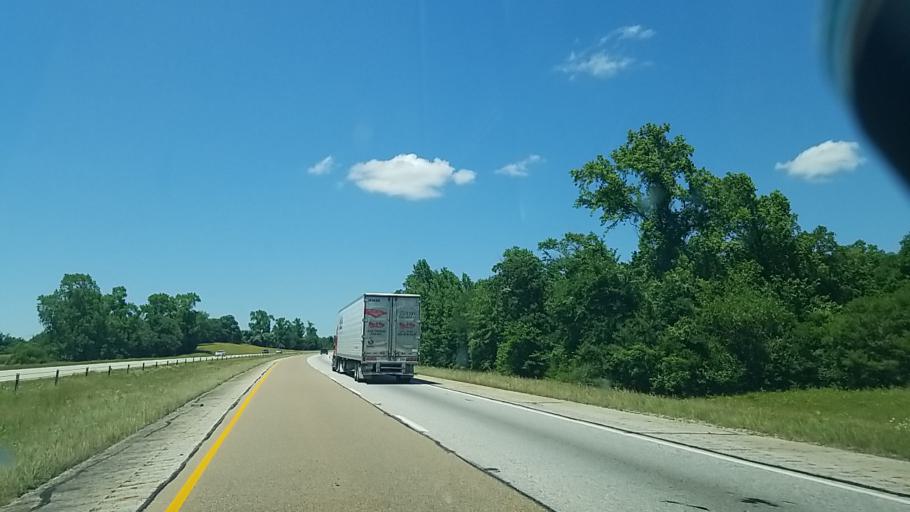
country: US
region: Texas
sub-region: Leon County
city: Centerville
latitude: 31.2084
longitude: -95.9964
